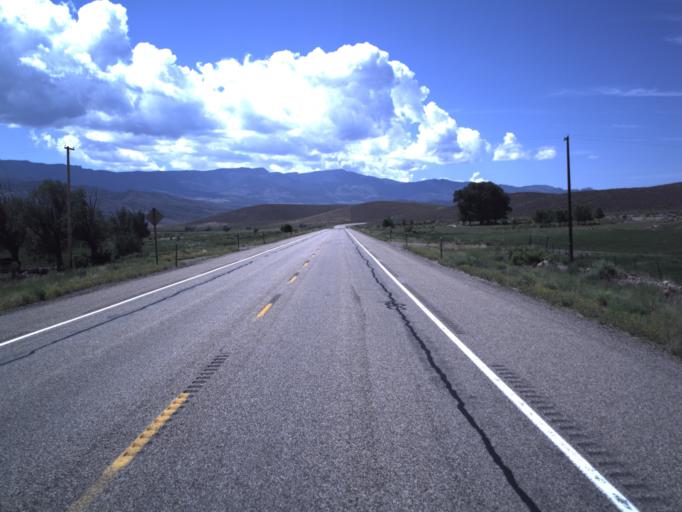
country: US
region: Utah
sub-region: Piute County
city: Junction
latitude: 38.2274
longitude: -112.2198
